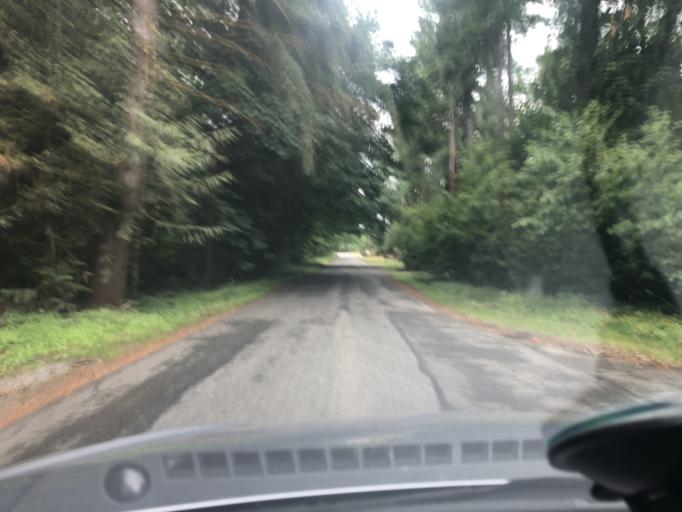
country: US
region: Washington
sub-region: King County
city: Black Diamond
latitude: 47.3224
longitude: -122.0352
